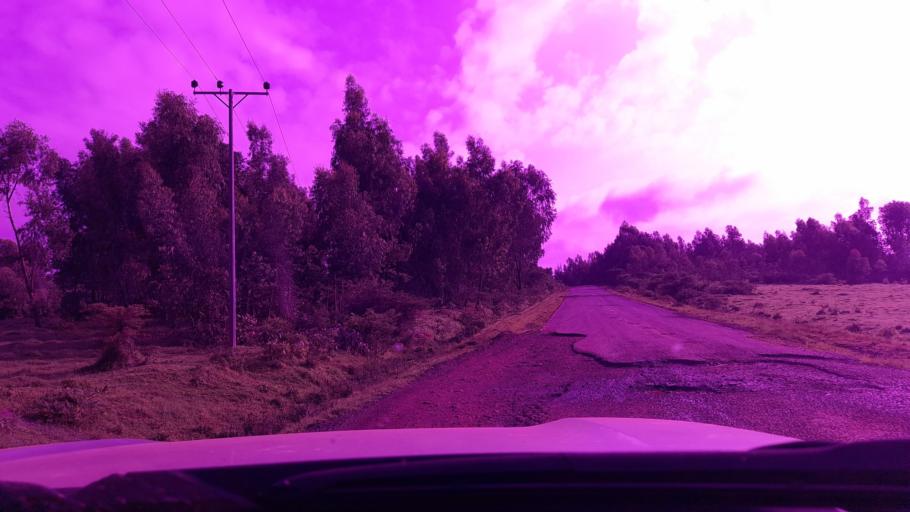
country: ET
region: Oromiya
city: Bedele
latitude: 8.2092
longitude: 36.4439
